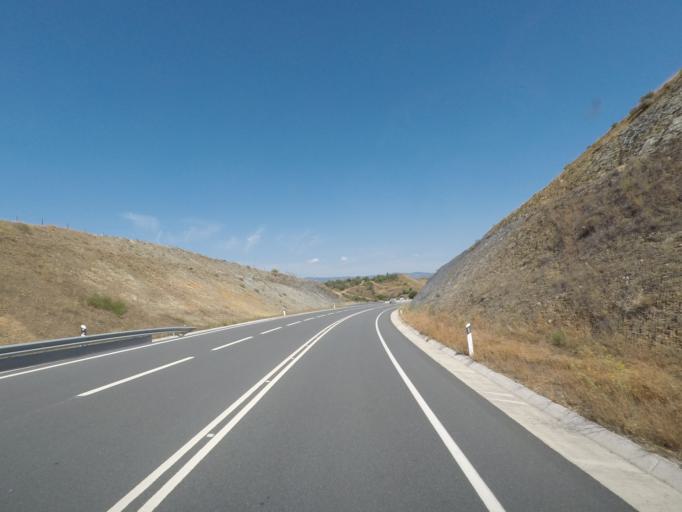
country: PT
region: Braganca
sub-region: Alfandega da Fe
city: Alfandega da Fe
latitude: 41.2886
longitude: -6.8954
